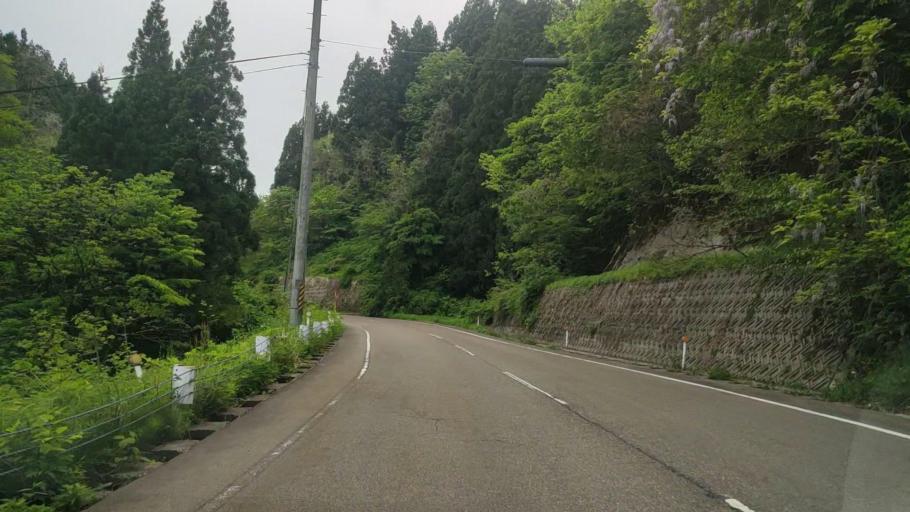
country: JP
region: Niigata
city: Gosen
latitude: 37.7147
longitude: 139.1126
